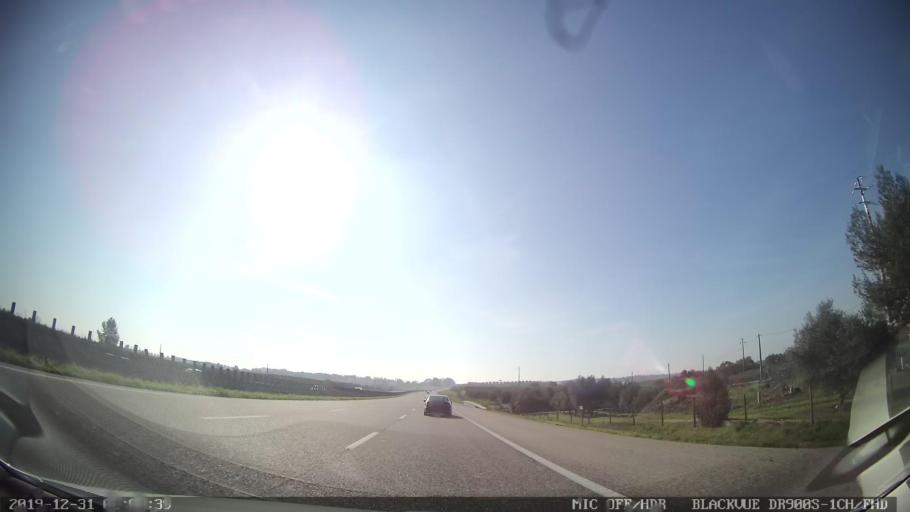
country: PT
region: Santarem
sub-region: Santarem
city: Santarem
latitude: 39.3237
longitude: -8.6627
